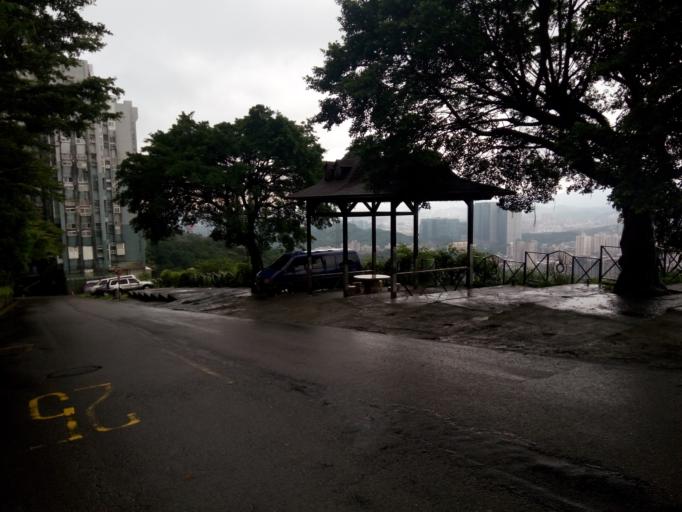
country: TW
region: Taiwan
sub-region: Keelung
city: Keelung
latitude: 25.0560
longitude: 121.6682
